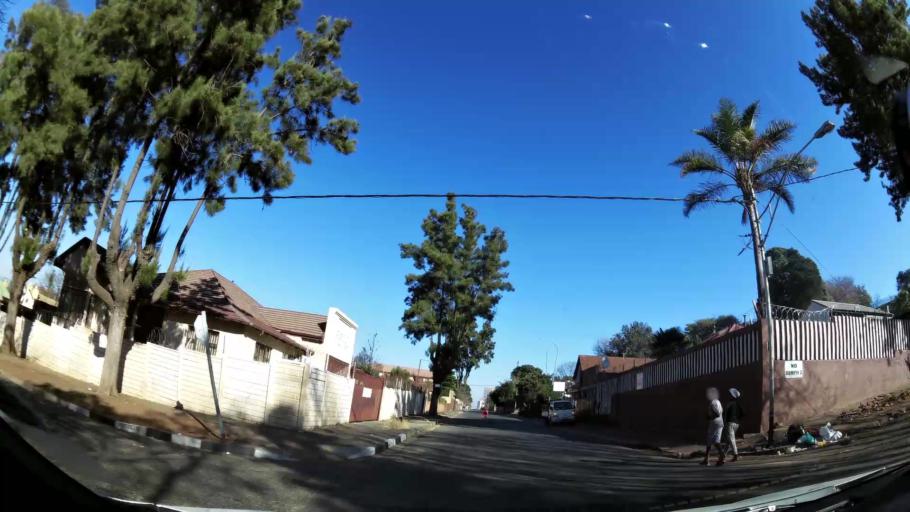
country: ZA
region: Gauteng
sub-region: City of Johannesburg Metropolitan Municipality
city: Johannesburg
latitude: -26.2028
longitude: 28.0774
